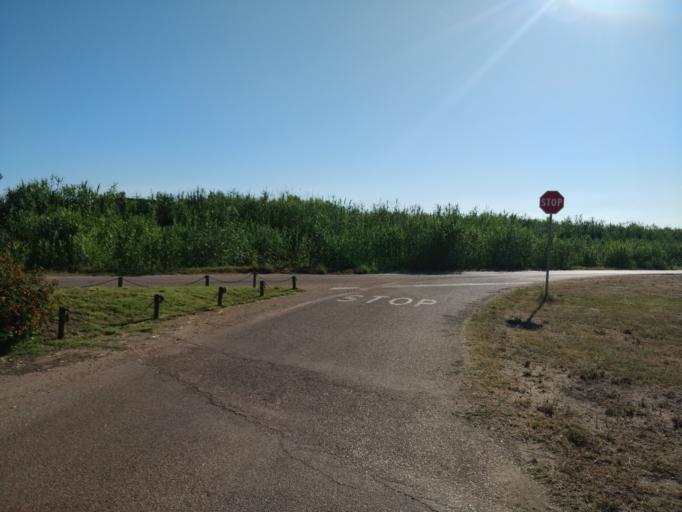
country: IT
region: Sardinia
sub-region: Provincia di Ogliastra
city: Lotzorai
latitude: 39.9609
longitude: 9.6775
